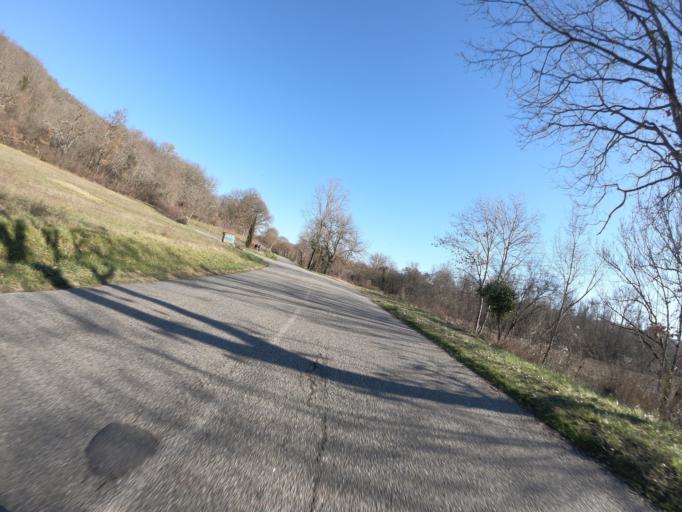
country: FR
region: Midi-Pyrenees
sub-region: Departement de l'Ariege
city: Mirepoix
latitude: 43.0835
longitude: 1.8185
